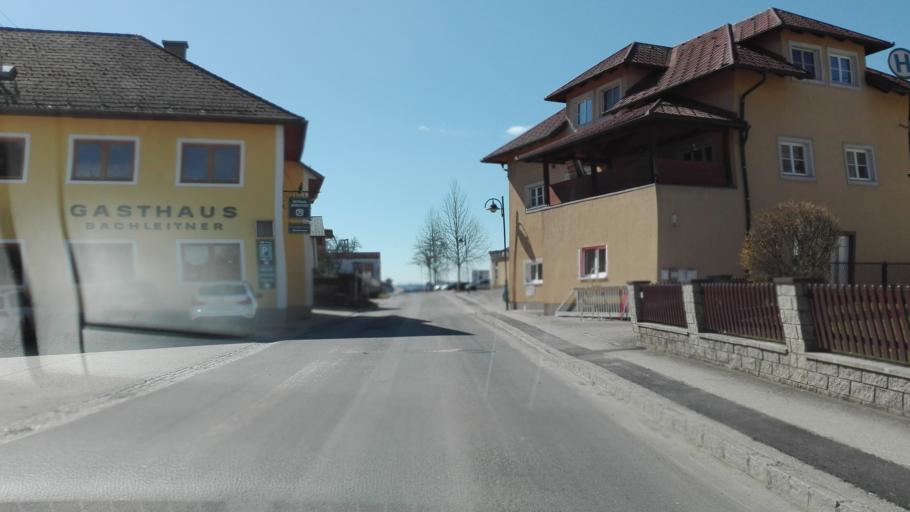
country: AT
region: Upper Austria
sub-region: Wels-Land
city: Buchkirchen
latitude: 48.2478
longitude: 13.9784
